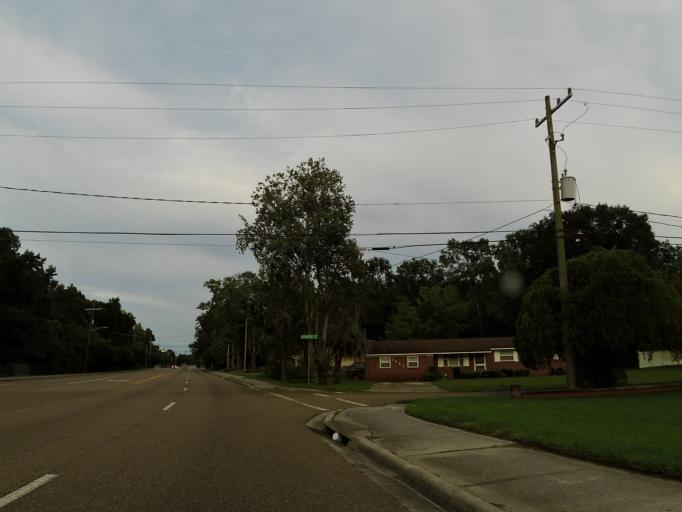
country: US
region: Florida
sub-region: Duval County
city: Jacksonville
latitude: 30.3899
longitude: -81.7266
